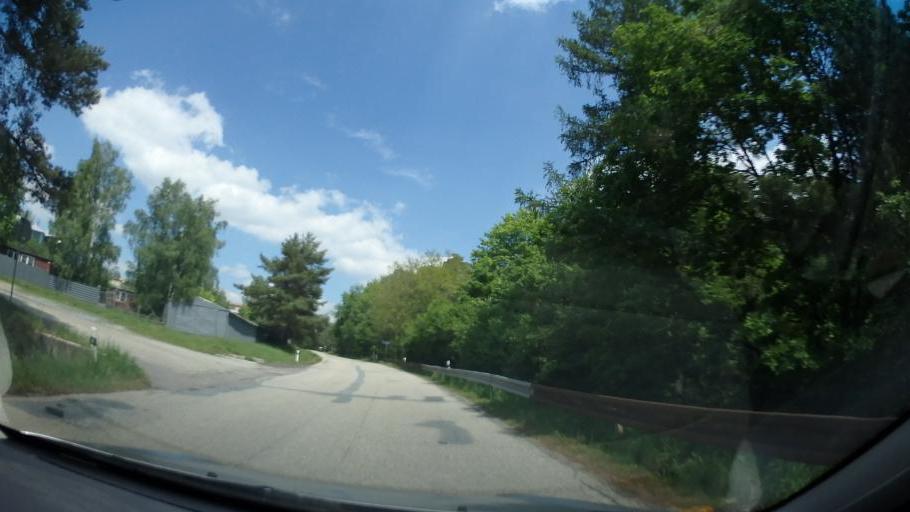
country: CZ
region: Vysocina
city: Rouchovany
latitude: 49.1284
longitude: 16.1276
